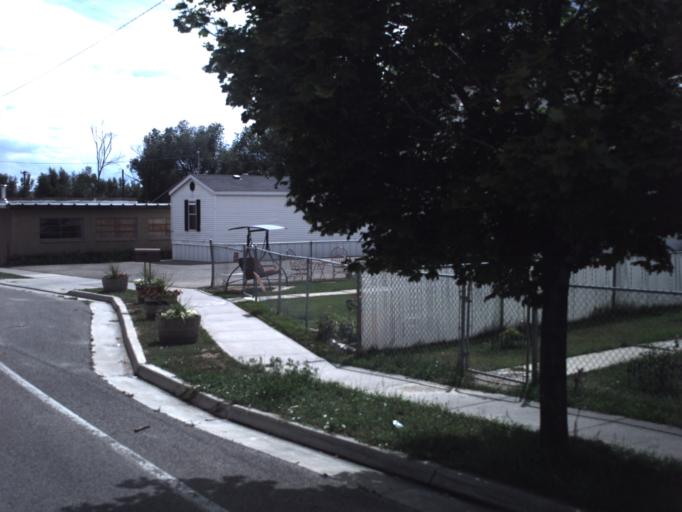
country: US
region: Utah
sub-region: Carbon County
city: Price
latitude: 39.5921
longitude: -110.8113
